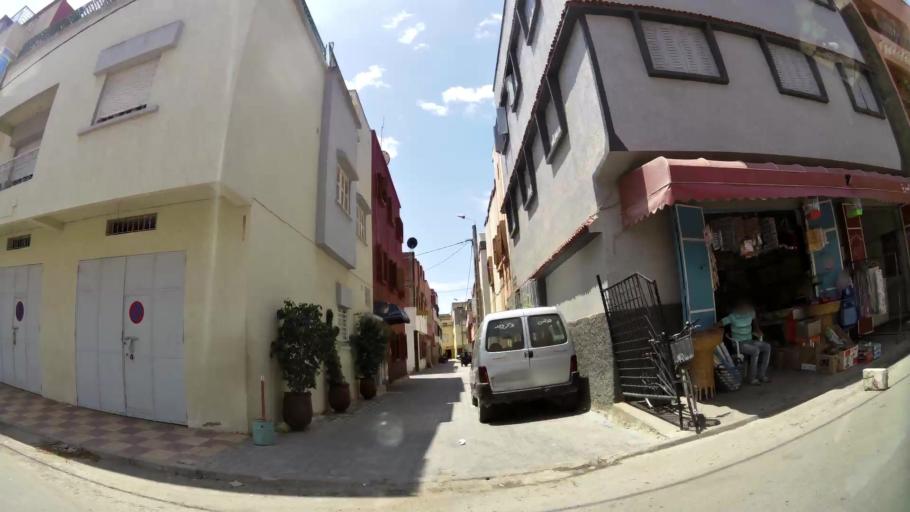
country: MA
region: Gharb-Chrarda-Beni Hssen
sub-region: Kenitra Province
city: Kenitra
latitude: 34.2699
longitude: -6.6026
